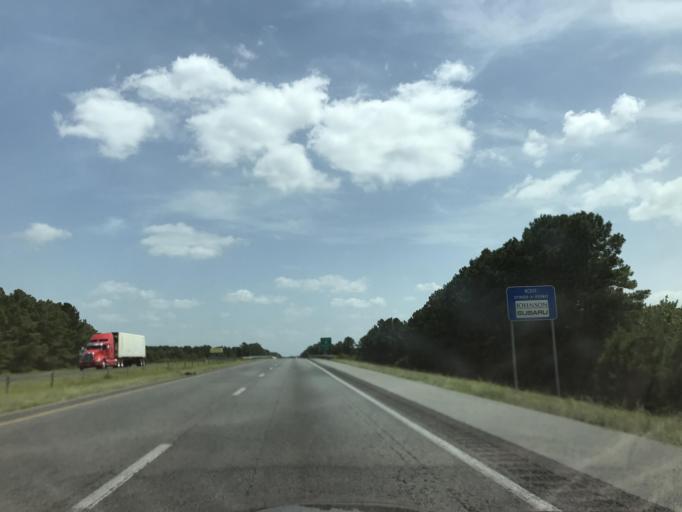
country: US
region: North Carolina
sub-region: Duplin County
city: Wallace
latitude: 34.7709
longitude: -77.9665
